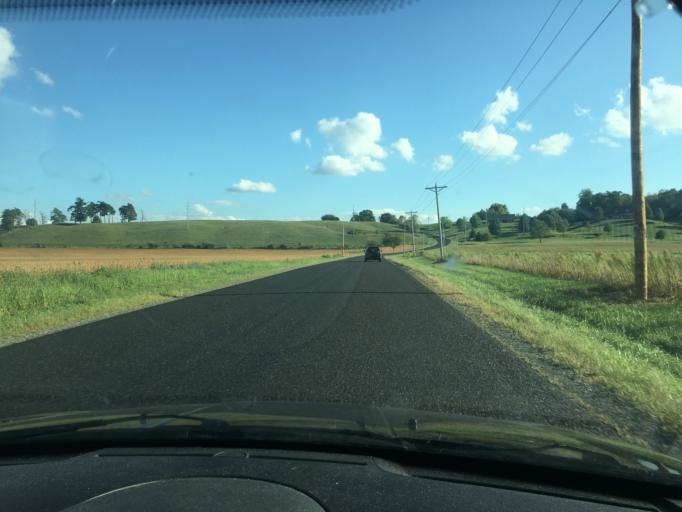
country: US
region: Ohio
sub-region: Logan County
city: West Liberty
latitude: 40.2749
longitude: -83.7237
